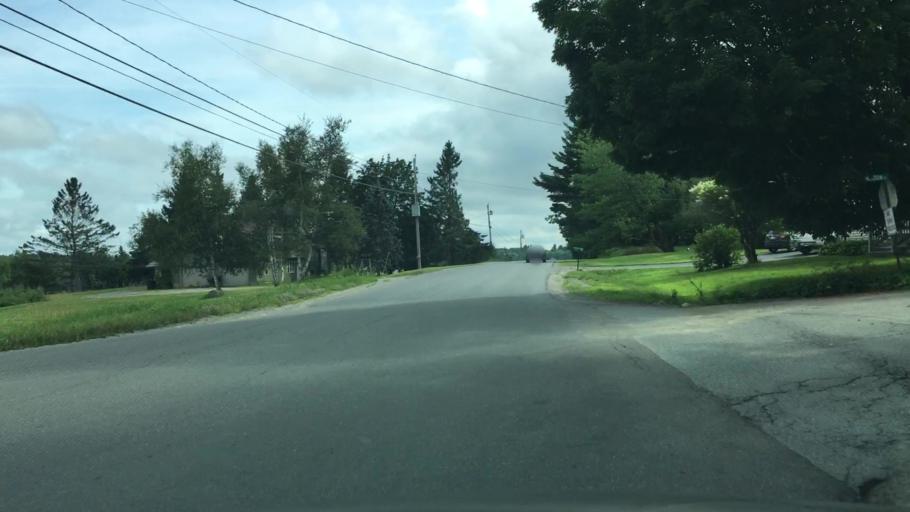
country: US
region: Maine
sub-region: Waldo County
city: Winterport
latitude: 44.6794
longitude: -68.8676
